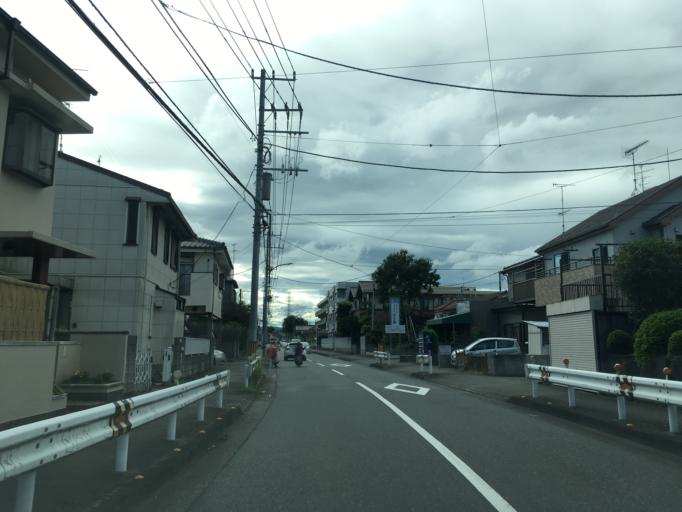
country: JP
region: Tokyo
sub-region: Machida-shi
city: Machida
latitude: 35.5607
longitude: 139.4087
